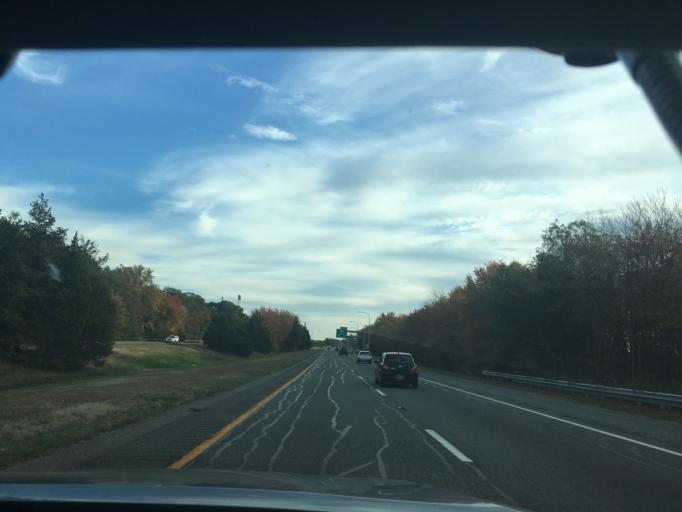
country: US
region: Rhode Island
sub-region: Providence County
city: Johnston
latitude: 41.7950
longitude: -71.5092
